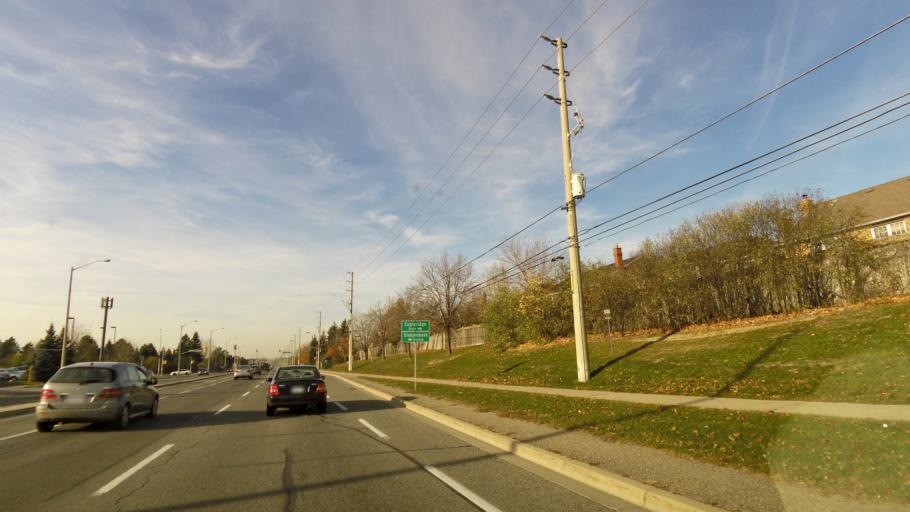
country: CA
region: Ontario
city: Brampton
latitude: 43.7607
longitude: -79.7423
